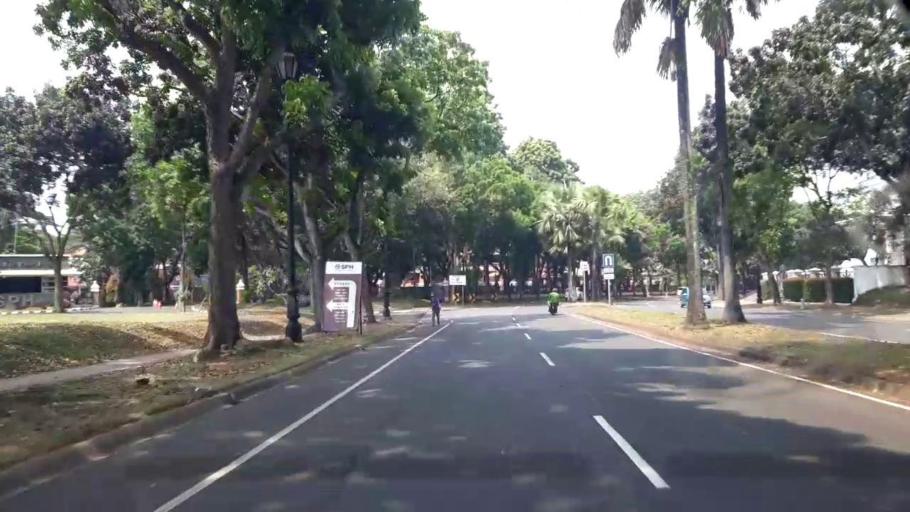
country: ID
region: Banten
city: Curug
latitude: -6.2390
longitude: 106.6074
